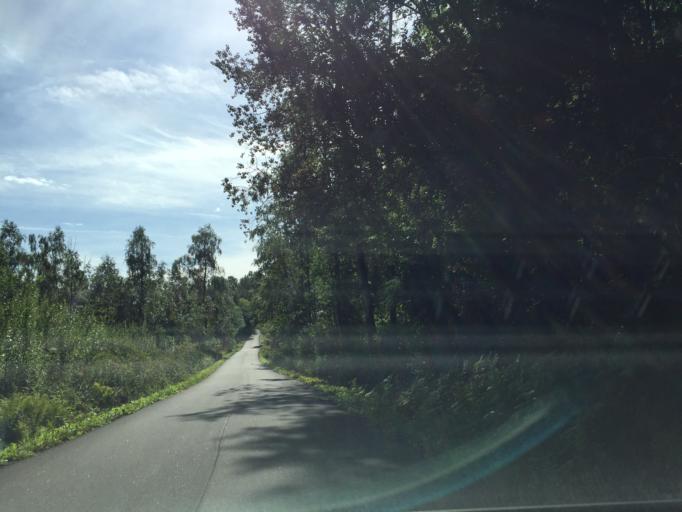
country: NO
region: Vestfold
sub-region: Hof
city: Hof
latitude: 59.4674
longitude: 10.1452
